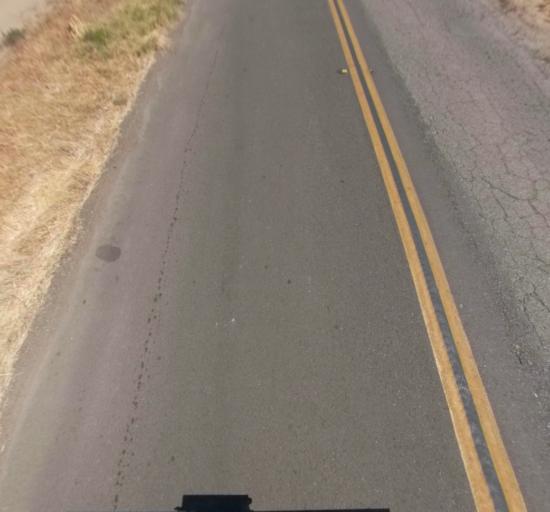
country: US
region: California
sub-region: Madera County
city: Madera
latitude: 36.9507
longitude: -120.1012
